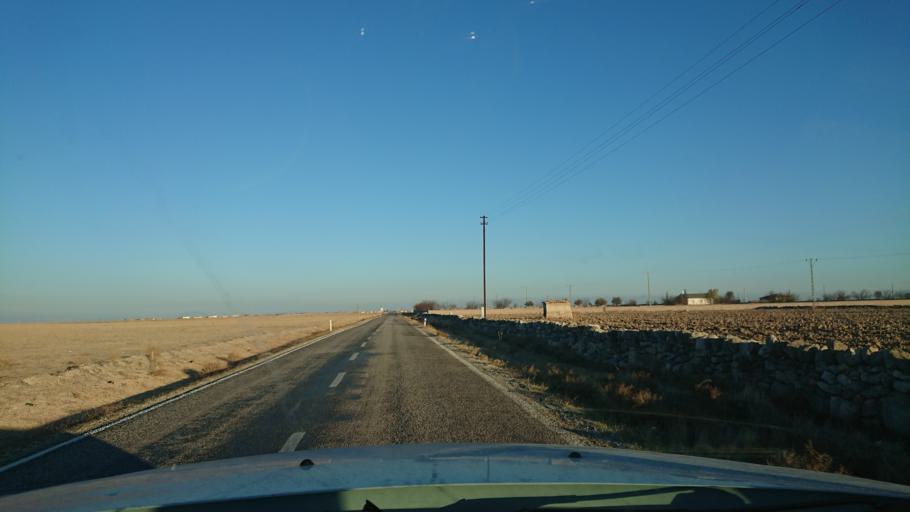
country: TR
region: Aksaray
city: Eskil
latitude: 38.4643
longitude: 33.2283
